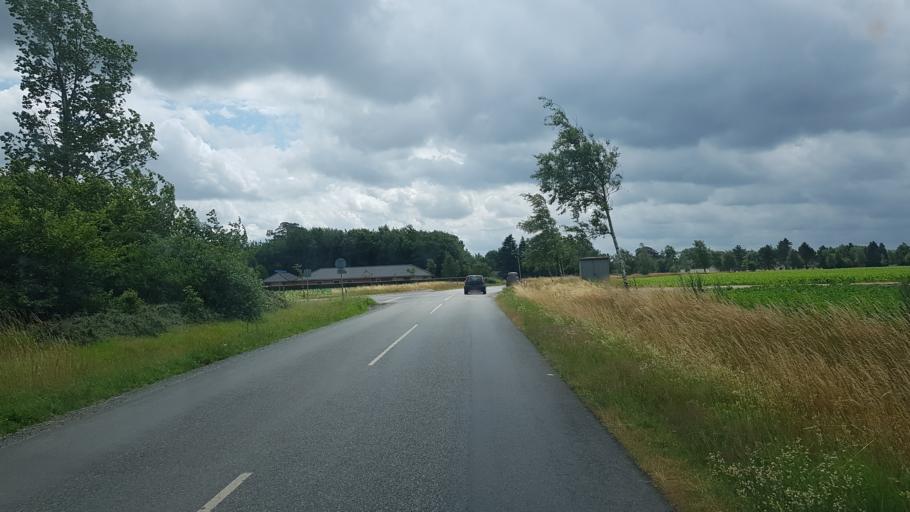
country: DK
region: South Denmark
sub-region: Kolding Kommune
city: Lunderskov
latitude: 55.4642
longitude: 9.2902
